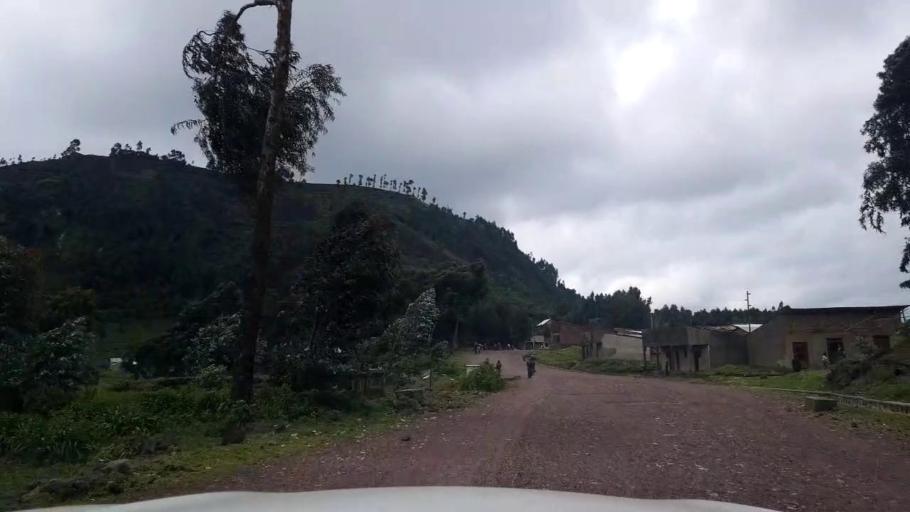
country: RW
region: Northern Province
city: Musanze
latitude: -1.5895
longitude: 29.4685
